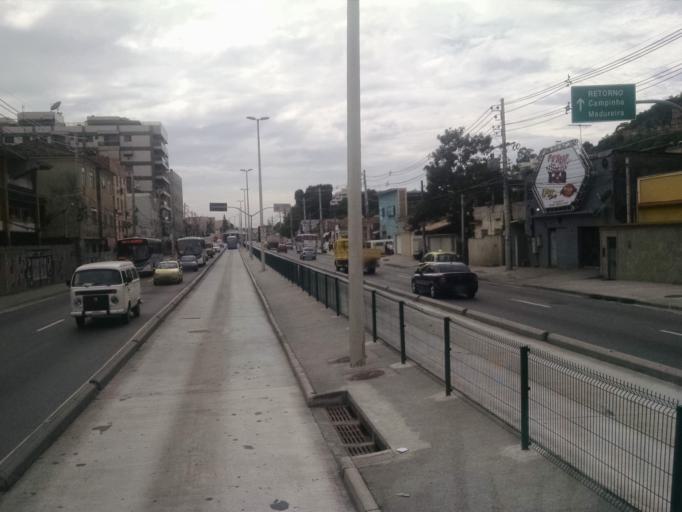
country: BR
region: Rio de Janeiro
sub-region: Sao Joao De Meriti
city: Sao Joao de Meriti
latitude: -22.8911
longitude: -43.3477
